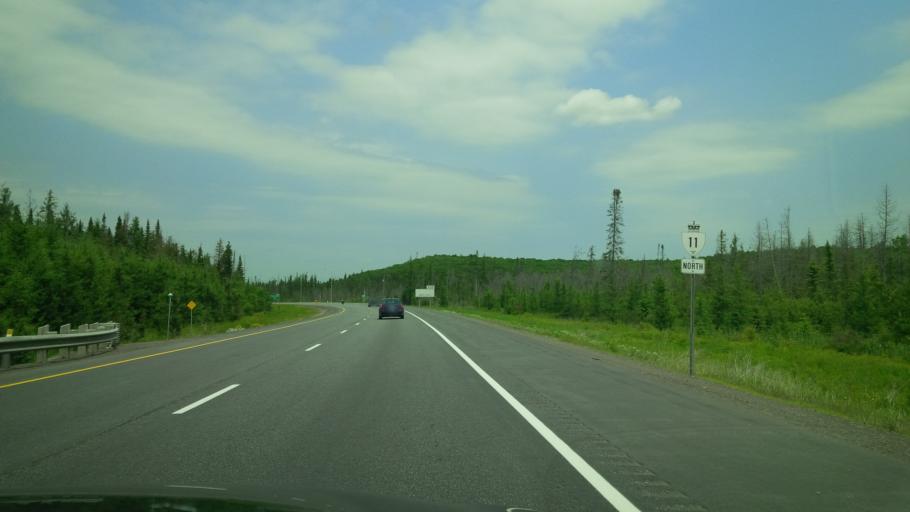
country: CA
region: Ontario
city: Huntsville
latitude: 45.4291
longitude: -79.2385
